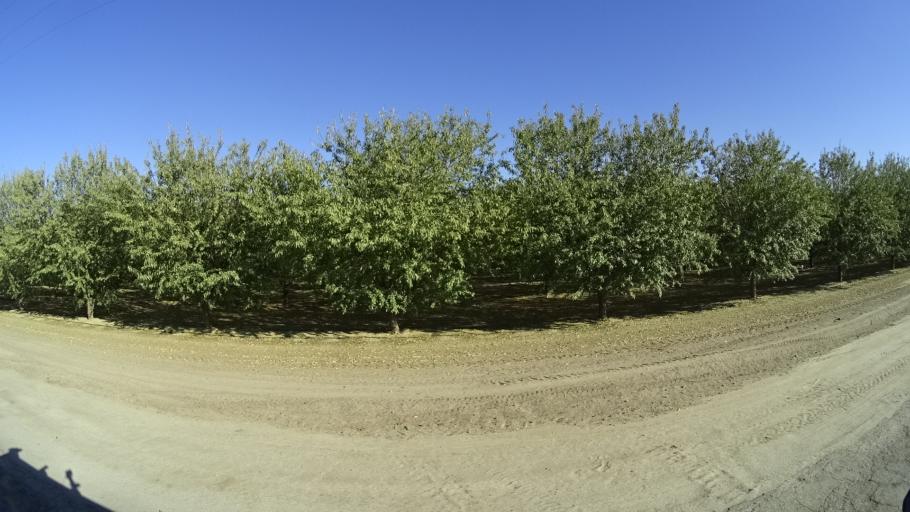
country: US
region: California
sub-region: Kern County
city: Greenacres
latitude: 35.2703
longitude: -119.1187
